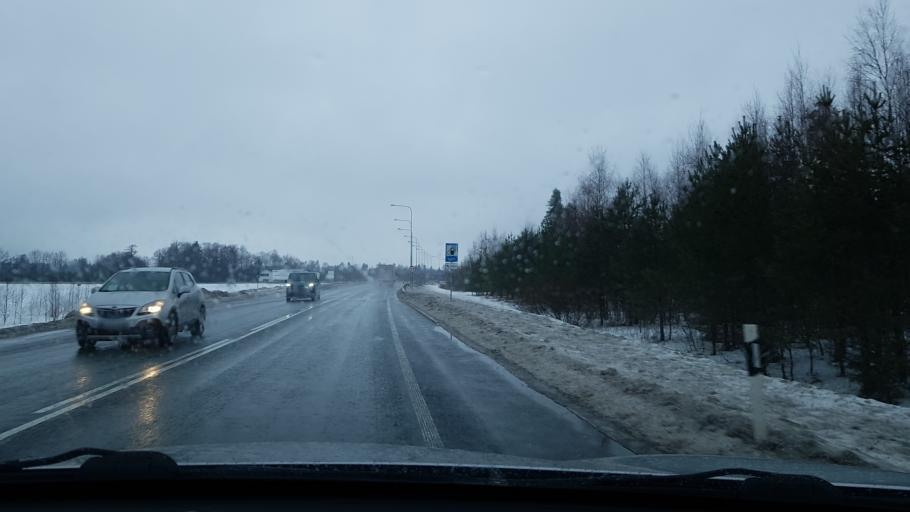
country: EE
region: Raplamaa
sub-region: Kohila vald
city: Kohila
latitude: 59.1676
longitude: 24.7717
